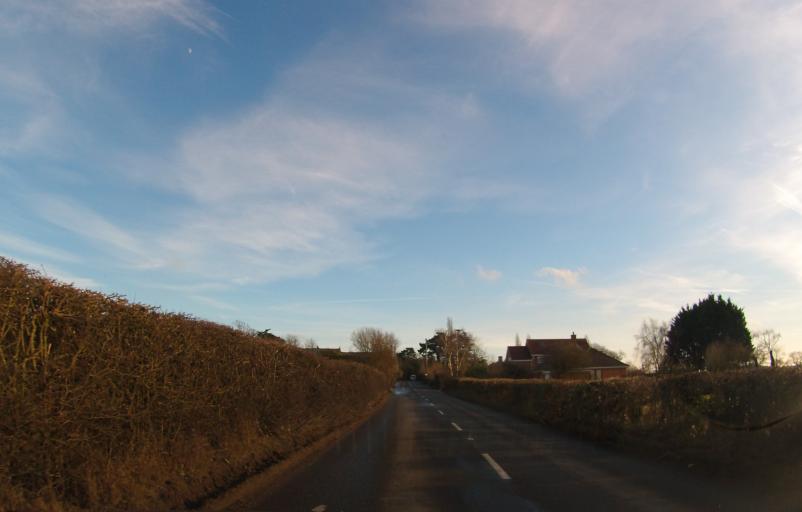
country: GB
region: England
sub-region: Isle of Wight
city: Newport
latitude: 50.7192
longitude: -1.2495
